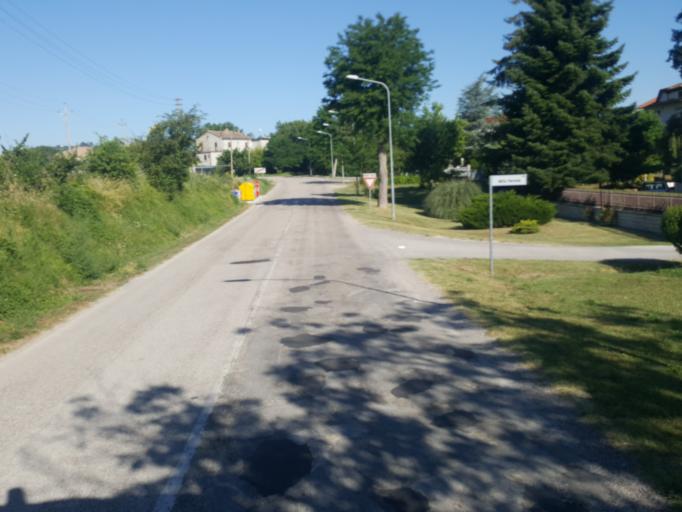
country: IT
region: The Marches
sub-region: Provincia di Pesaro e Urbino
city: Montecalvo in Foglia
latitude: 43.7849
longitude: 12.6284
